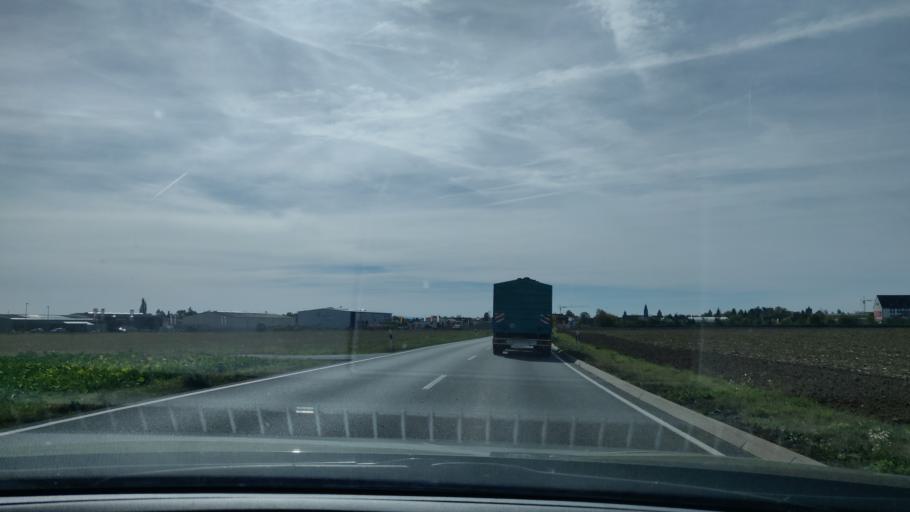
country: DE
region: Hesse
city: Fritzlar
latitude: 51.1441
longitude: 9.2740
